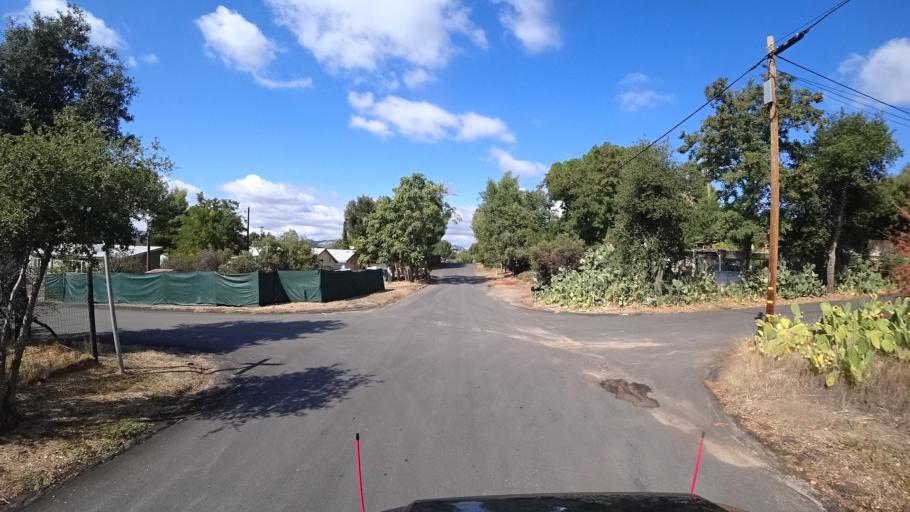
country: US
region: California
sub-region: San Diego County
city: Campo
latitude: 32.6789
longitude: -116.5014
